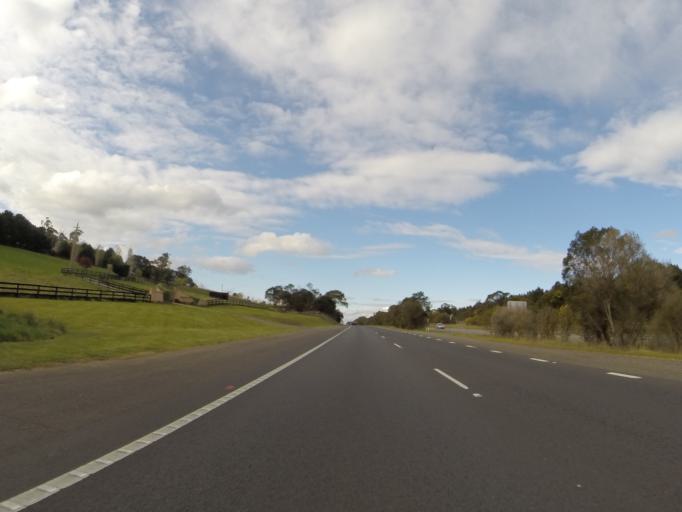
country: AU
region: New South Wales
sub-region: Wingecarribee
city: Bundanoon
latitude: -34.6024
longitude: 150.2338
